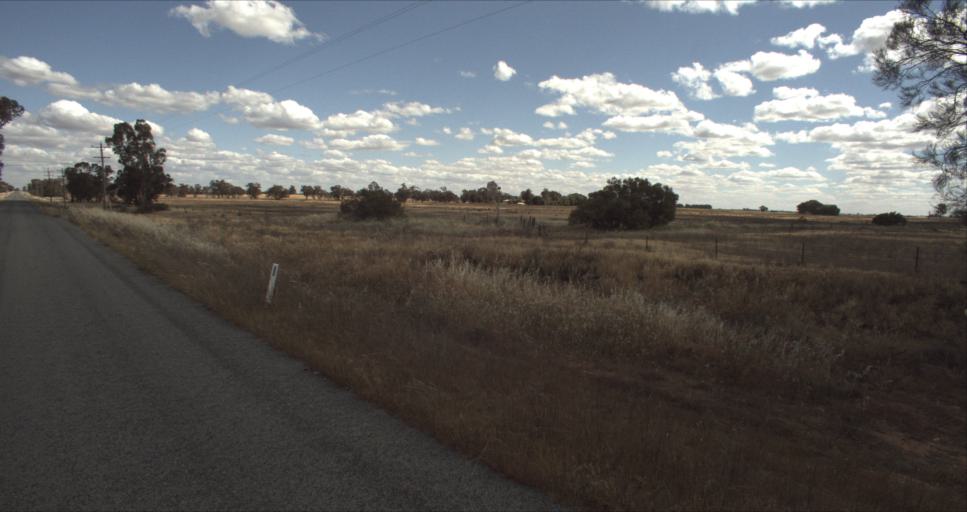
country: AU
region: New South Wales
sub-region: Leeton
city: Leeton
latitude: -34.4838
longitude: 146.2486
